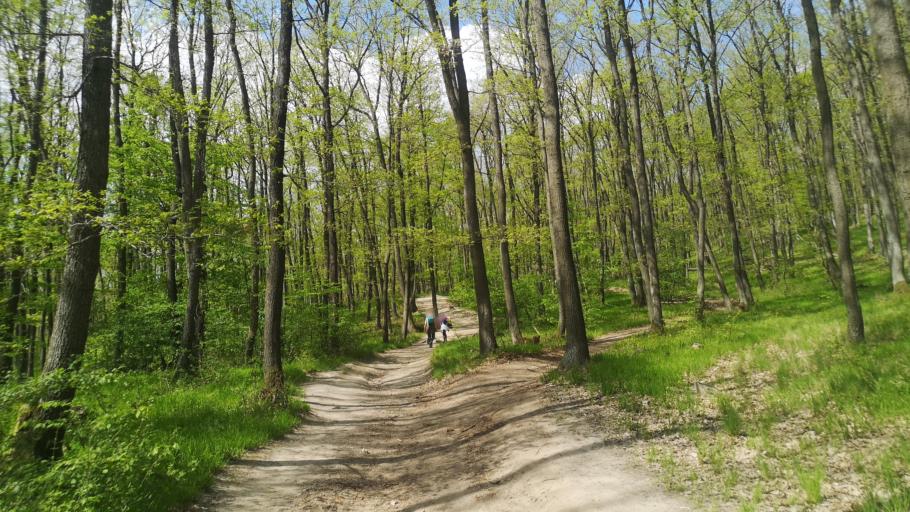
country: SK
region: Nitriansky
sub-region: Okres Nitra
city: Nitra
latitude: 48.4046
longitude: 18.2133
